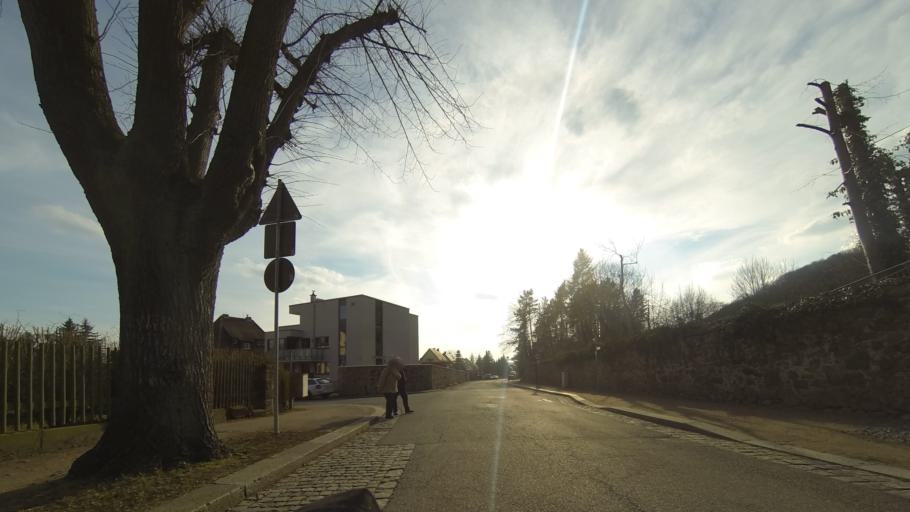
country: DE
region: Saxony
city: Radebeul
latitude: 51.1102
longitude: 13.6893
